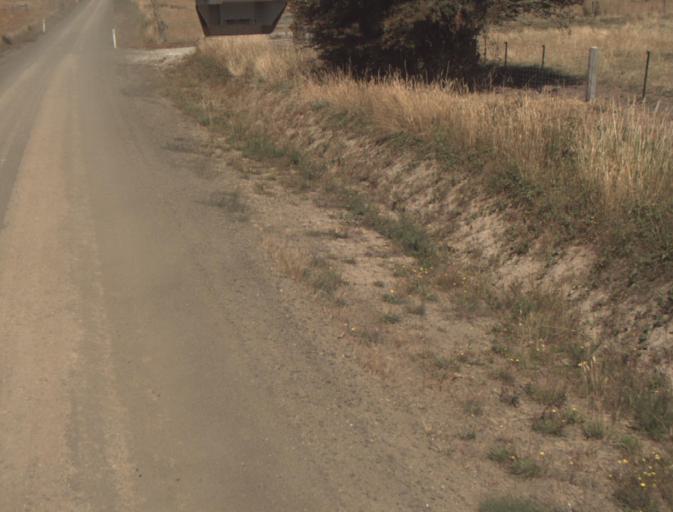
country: AU
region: Tasmania
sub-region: Launceston
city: Mayfield
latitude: -41.2517
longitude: 147.1339
